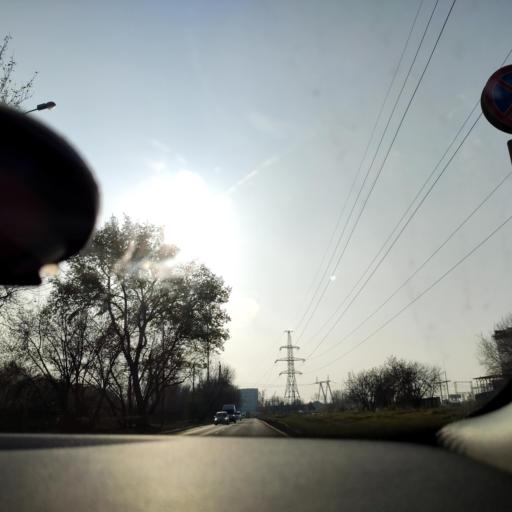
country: RU
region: Moscow
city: Kuz'minki
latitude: 55.6695
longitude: 37.8075
